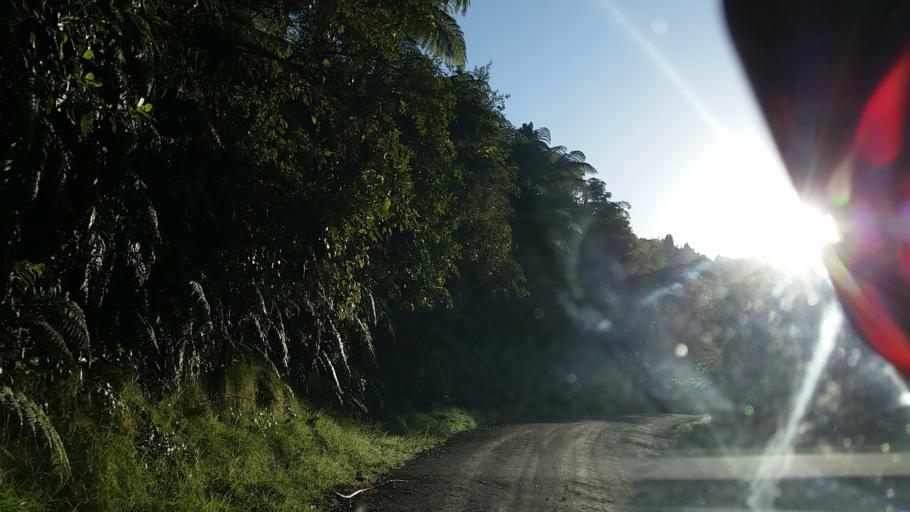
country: NZ
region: Bay of Plenty
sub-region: Rotorua District
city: Rotorua
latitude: -38.1591
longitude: 176.3618
